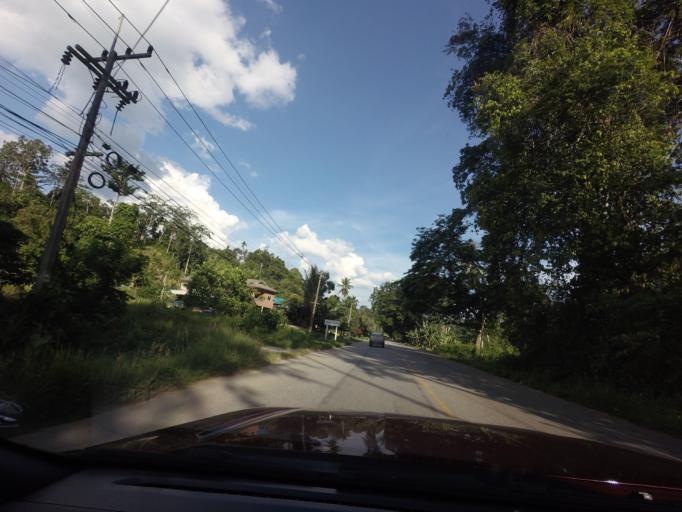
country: TH
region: Yala
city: Than To
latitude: 6.1755
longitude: 101.1764
